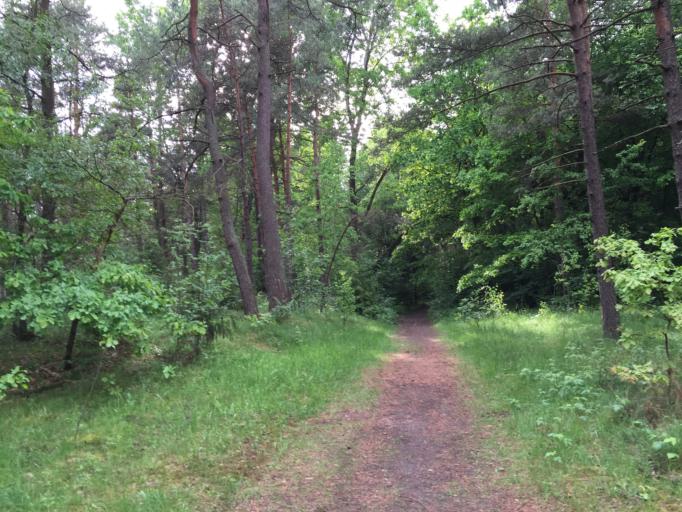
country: LT
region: Klaipedos apskritis
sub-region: Klaipeda
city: Klaipeda
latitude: 55.7477
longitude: 21.1231
